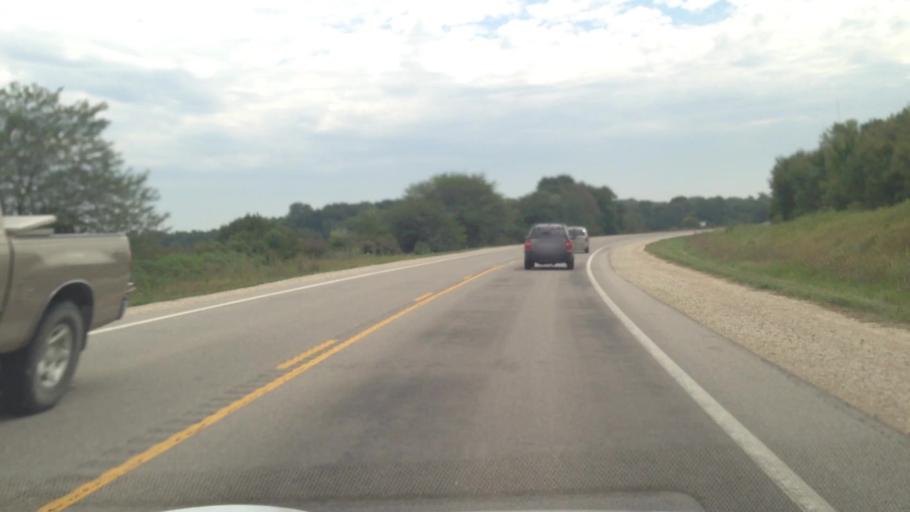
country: US
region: Kansas
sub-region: Allen County
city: Iola
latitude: 37.9145
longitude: -95.1405
